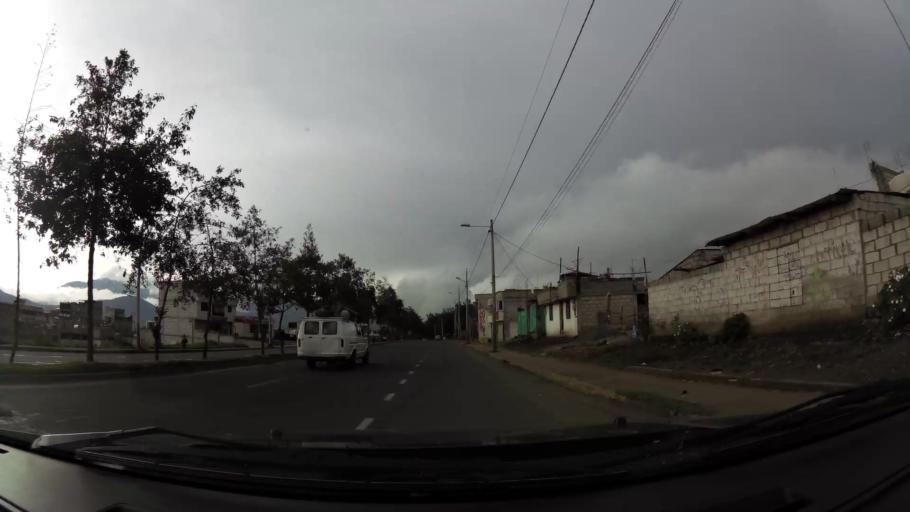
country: EC
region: Pichincha
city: Quito
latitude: -0.2922
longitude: -78.5196
